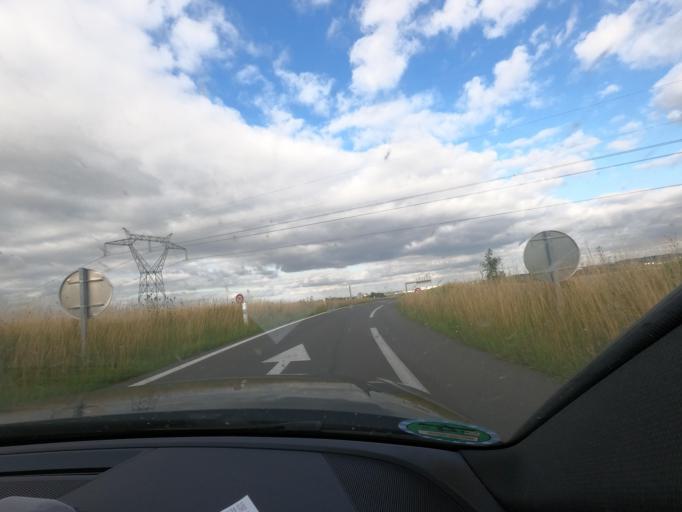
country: FR
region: Picardie
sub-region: Departement de la Somme
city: Pont-de-Metz
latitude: 49.8913
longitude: 2.2311
